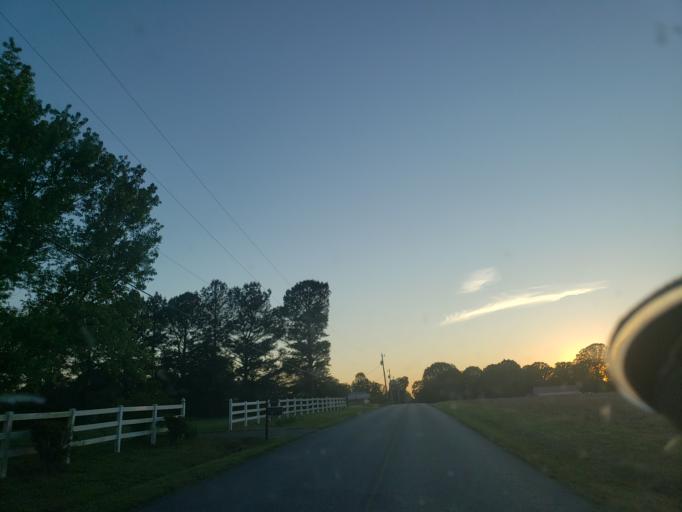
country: US
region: Alabama
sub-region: Madison County
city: Hazel Green
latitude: 34.9770
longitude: -86.6609
